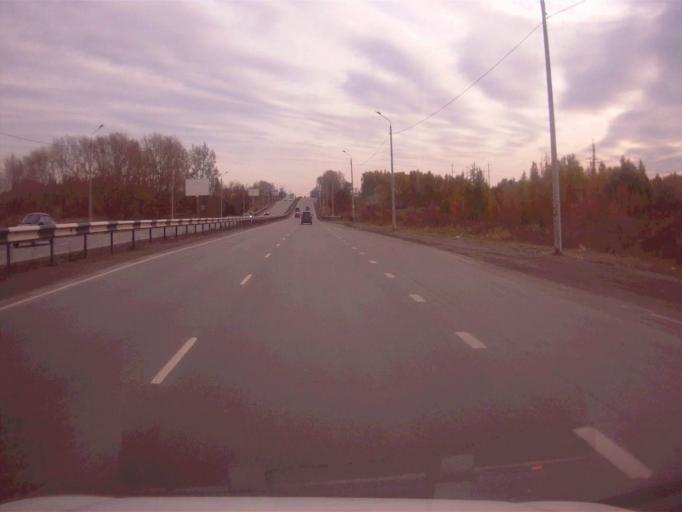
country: RU
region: Chelyabinsk
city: Novosineglazovskiy
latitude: 55.0594
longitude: 61.4030
